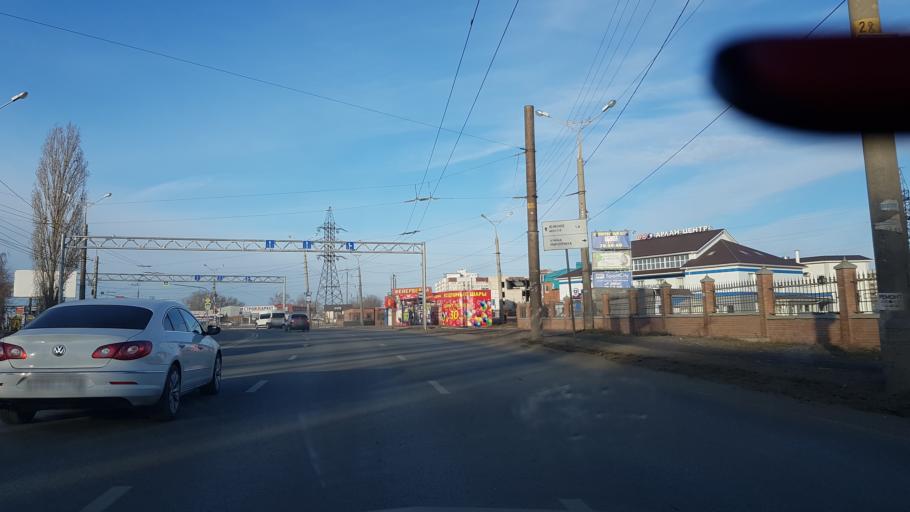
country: RU
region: Samara
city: Tol'yatti
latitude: 53.5345
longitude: 49.3955
